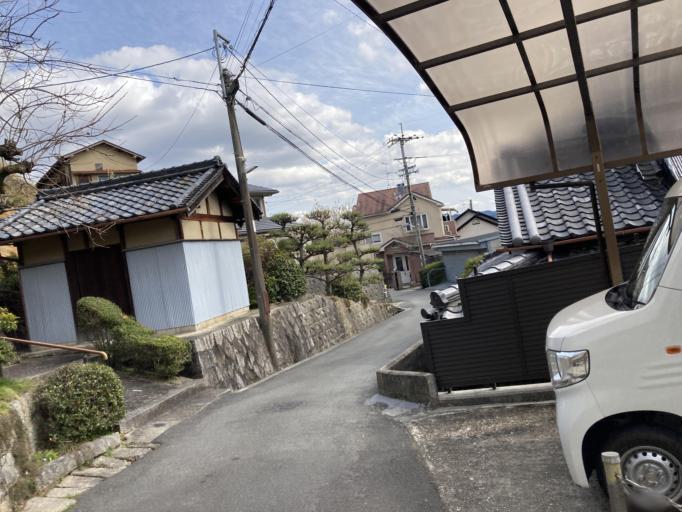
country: JP
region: Nara
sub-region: Ikoma-shi
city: Ikoma
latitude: 34.7057
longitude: 135.6937
